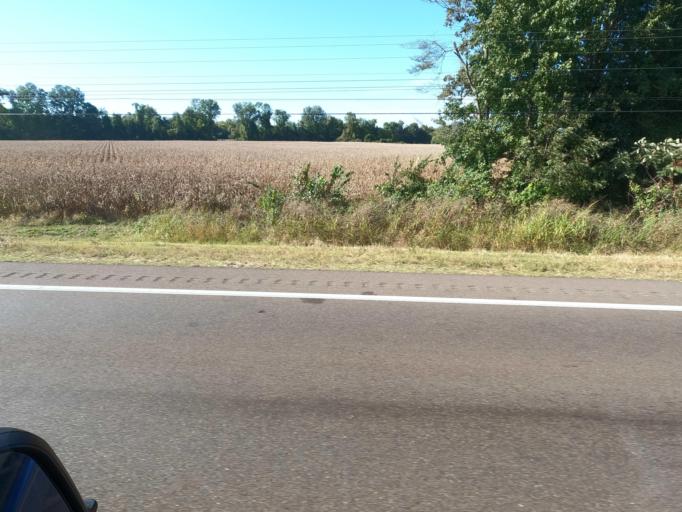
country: US
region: Tennessee
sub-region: Obion County
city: Englewood
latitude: 36.3645
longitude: -89.1296
